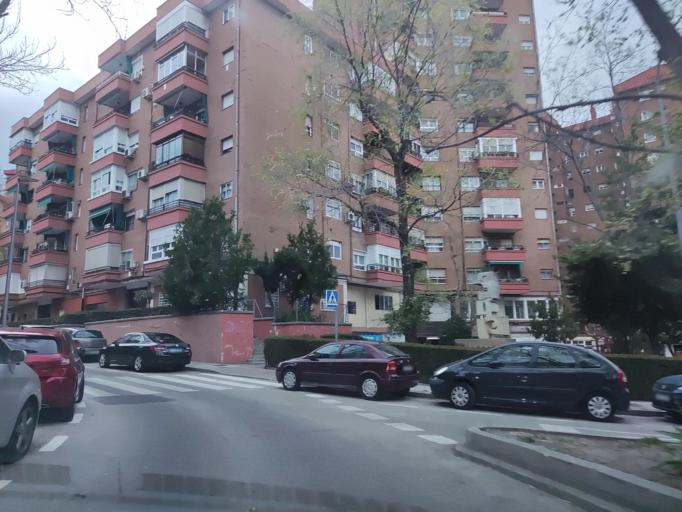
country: ES
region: Madrid
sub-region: Provincia de Madrid
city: Hortaleza
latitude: 40.4671
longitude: -3.6312
